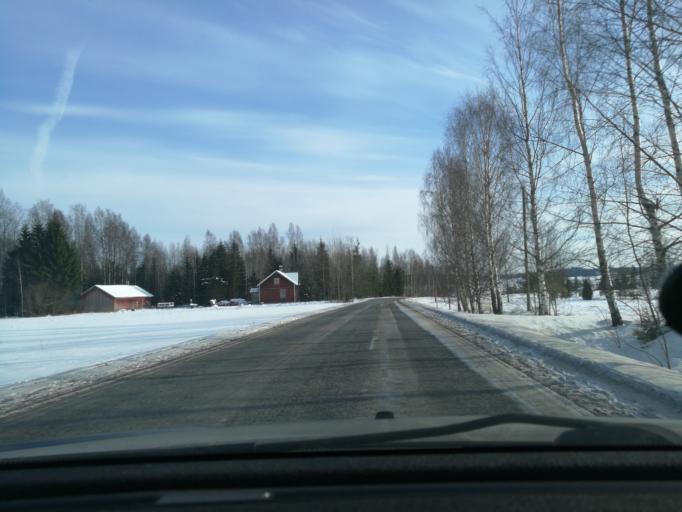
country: FI
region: Uusimaa
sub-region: Helsinki
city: Saukkola
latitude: 60.4440
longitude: 24.0144
